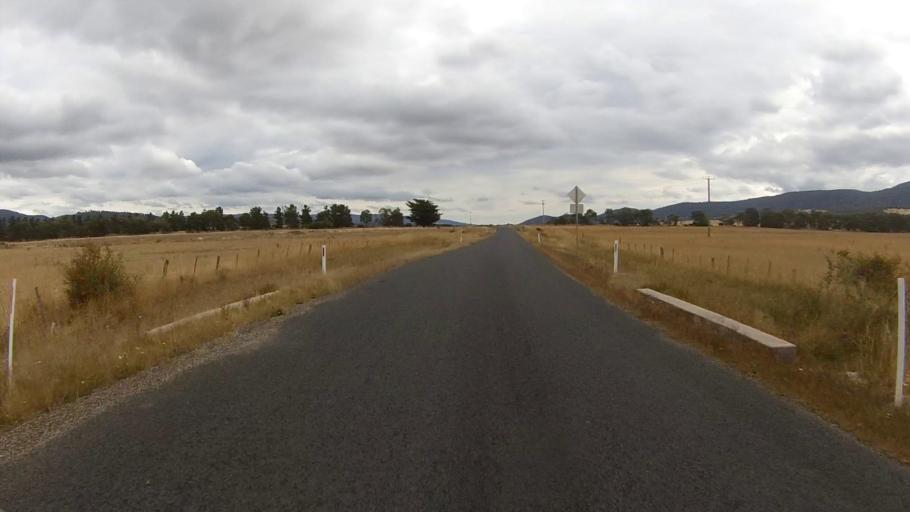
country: AU
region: Tasmania
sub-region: Break O'Day
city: St Helens
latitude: -41.8236
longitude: 147.8683
